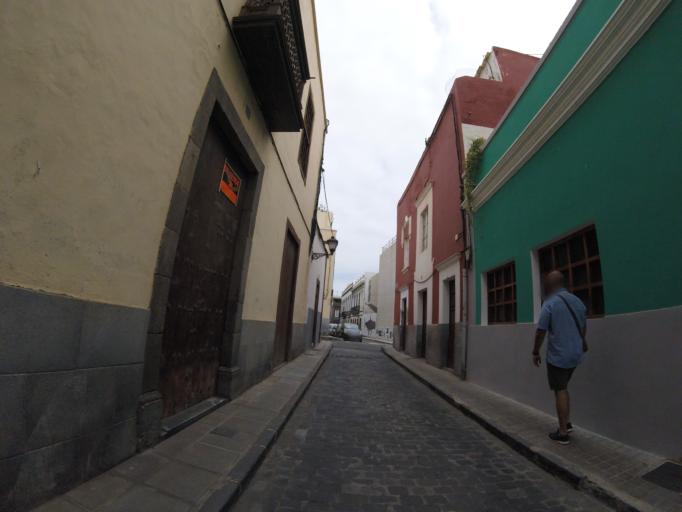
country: ES
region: Canary Islands
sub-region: Provincia de Las Palmas
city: Las Palmas de Gran Canaria
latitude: 28.0990
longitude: -15.4157
